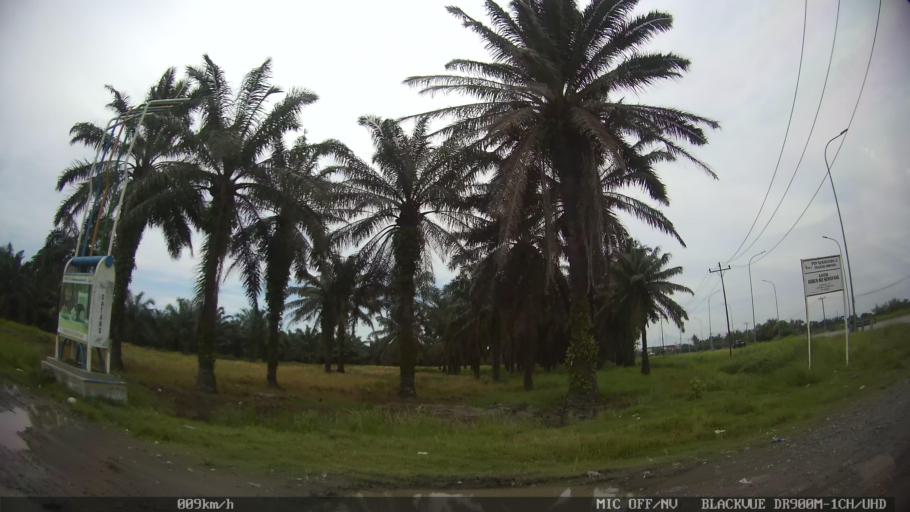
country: ID
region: North Sumatra
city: Sunggal
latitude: 3.6193
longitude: 98.5766
